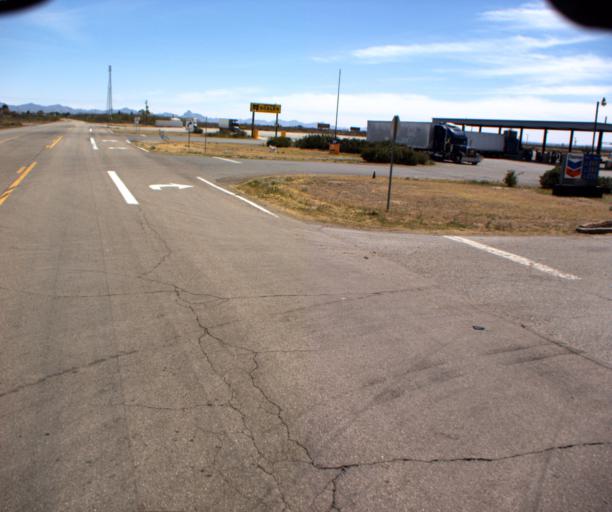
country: US
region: New Mexico
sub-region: Hidalgo County
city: Lordsburg
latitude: 32.2719
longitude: -109.2443
